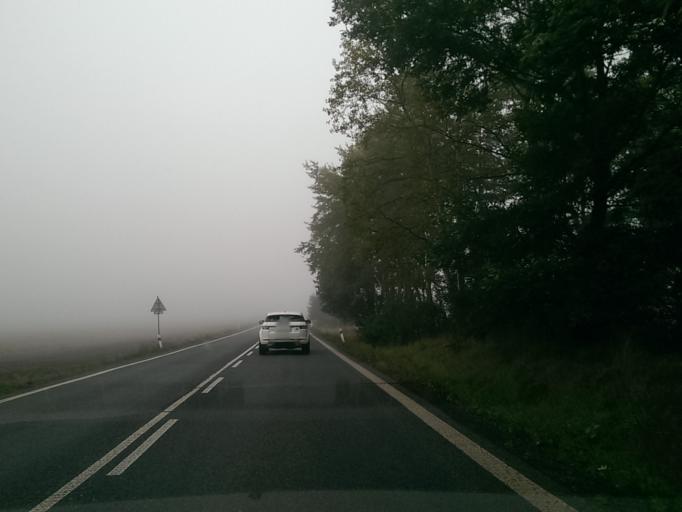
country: CZ
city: Doksy
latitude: 50.6026
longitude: 14.5913
